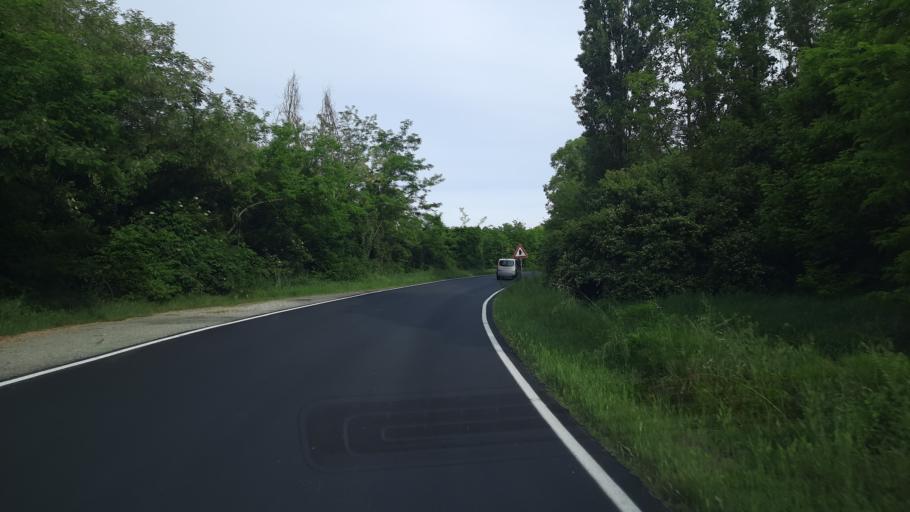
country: IT
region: Piedmont
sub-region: Provincia di Alessandria
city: Casale Monferrato
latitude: 45.1350
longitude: 8.4267
